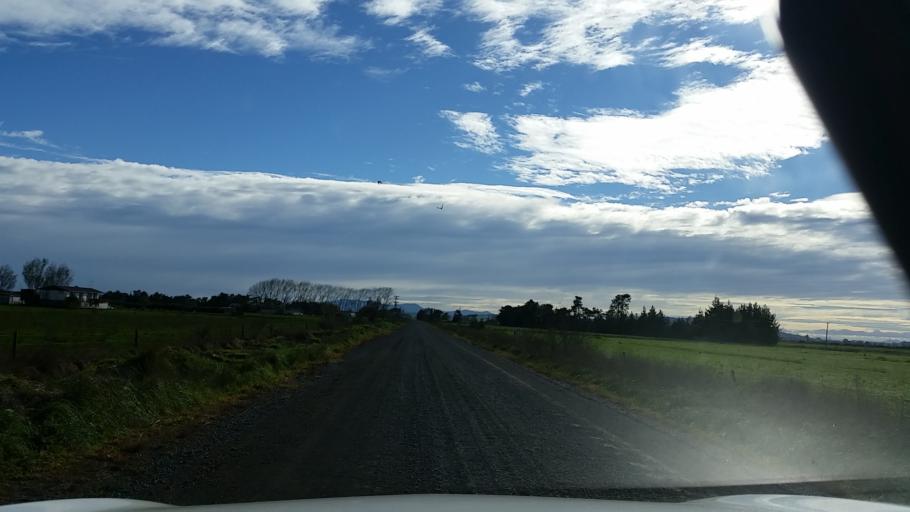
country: NZ
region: Waikato
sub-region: Hamilton City
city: Hamilton
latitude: -37.6725
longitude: 175.4409
